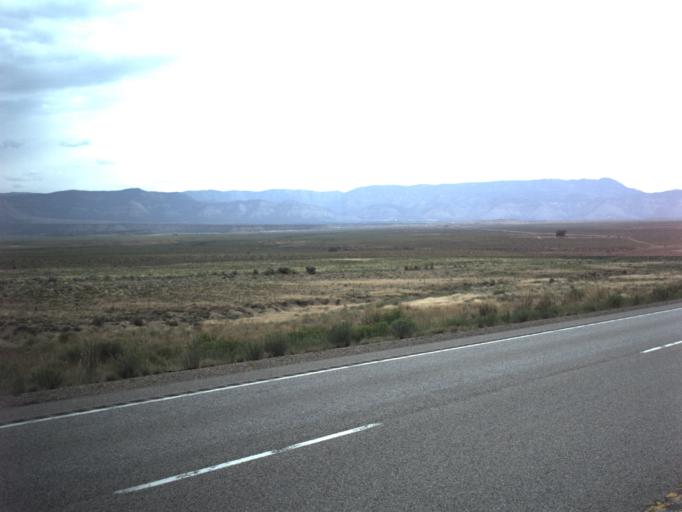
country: US
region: Utah
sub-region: Carbon County
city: Wellington
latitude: 39.5325
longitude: -110.5892
